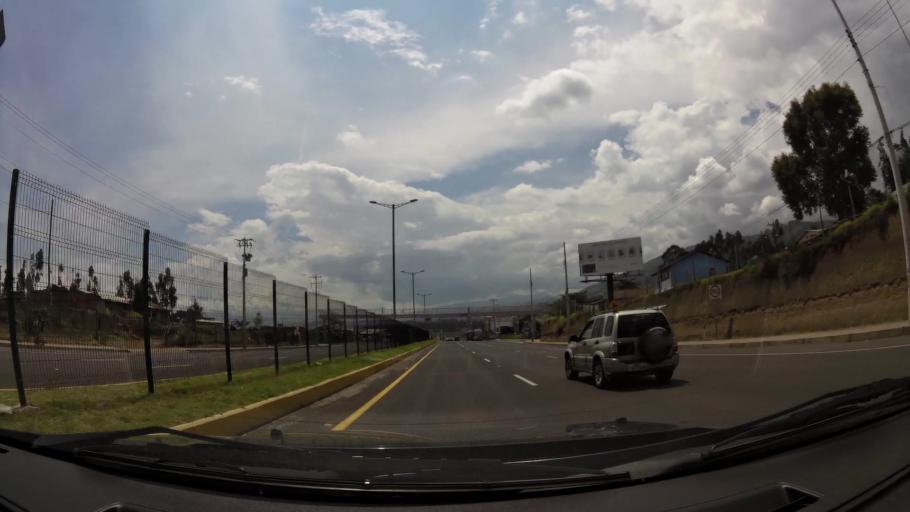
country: EC
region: Pichincha
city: Sangolqui
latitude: -0.2215
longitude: -78.3392
